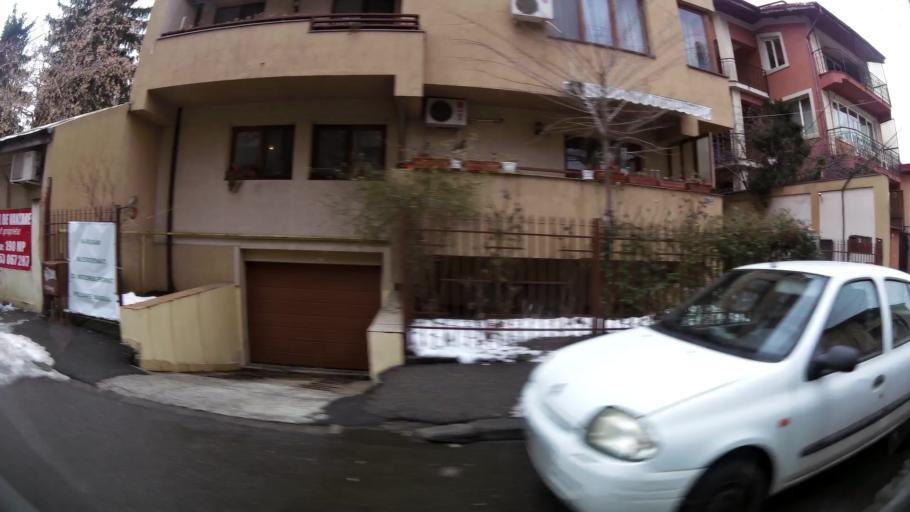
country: RO
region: Ilfov
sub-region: Comuna Chiajna
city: Rosu
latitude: 44.4673
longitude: 26.0559
